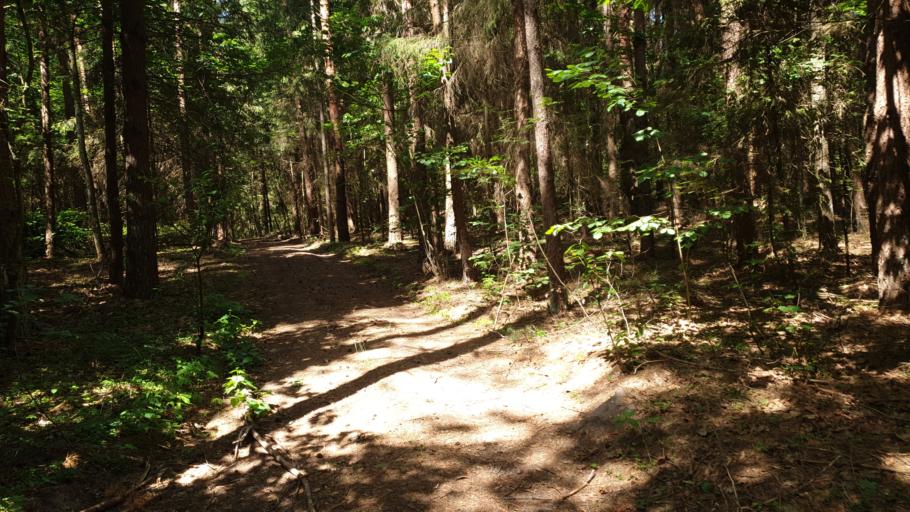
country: LT
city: Grigiskes
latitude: 54.7789
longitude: 24.9928
